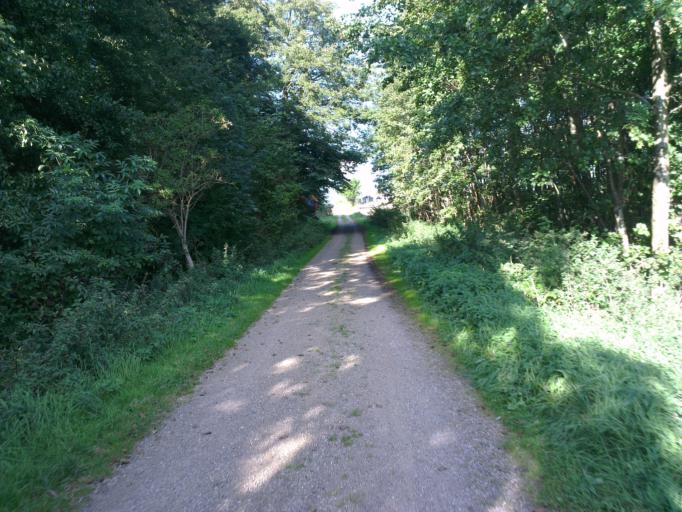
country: DK
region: Capital Region
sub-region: Frederikssund Kommune
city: Frederikssund
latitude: 55.8162
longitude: 12.0291
